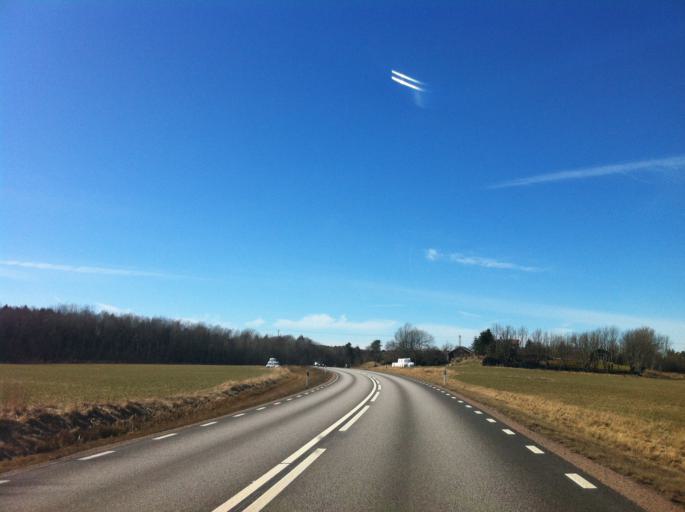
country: SE
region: Vaestra Goetaland
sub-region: Sotenas Kommun
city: Hunnebostrand
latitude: 58.4139
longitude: 11.3402
